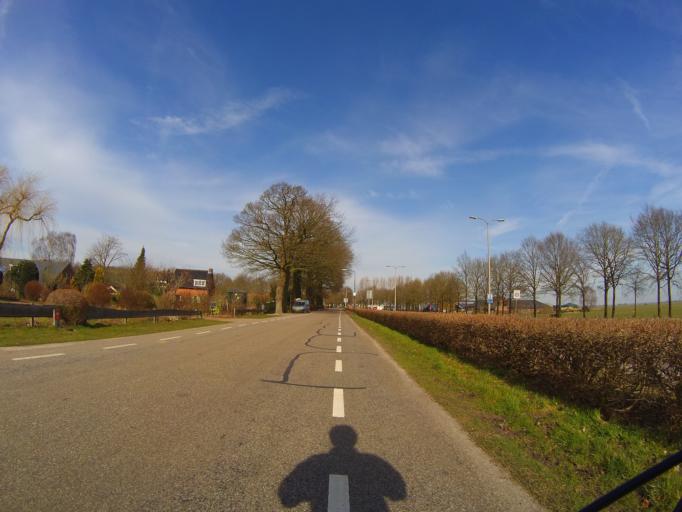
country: NL
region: Utrecht
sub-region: Gemeente Baarn
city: Baarn
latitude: 52.2266
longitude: 5.2565
